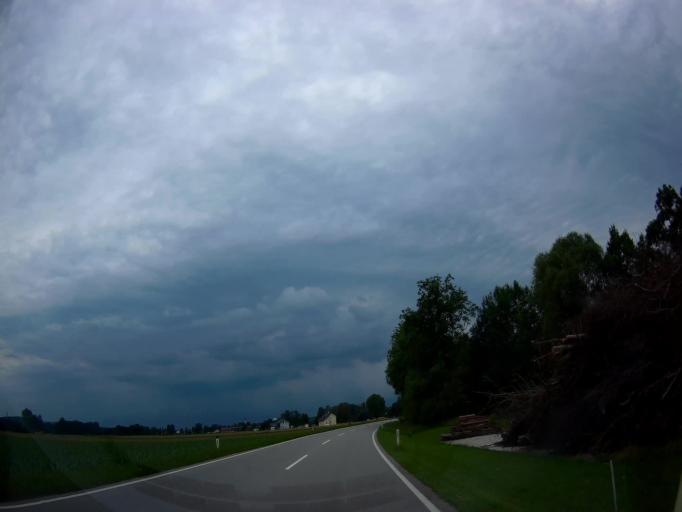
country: AT
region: Upper Austria
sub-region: Politischer Bezirk Braunau am Inn
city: Braunau am Inn
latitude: 48.1736
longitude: 13.1277
